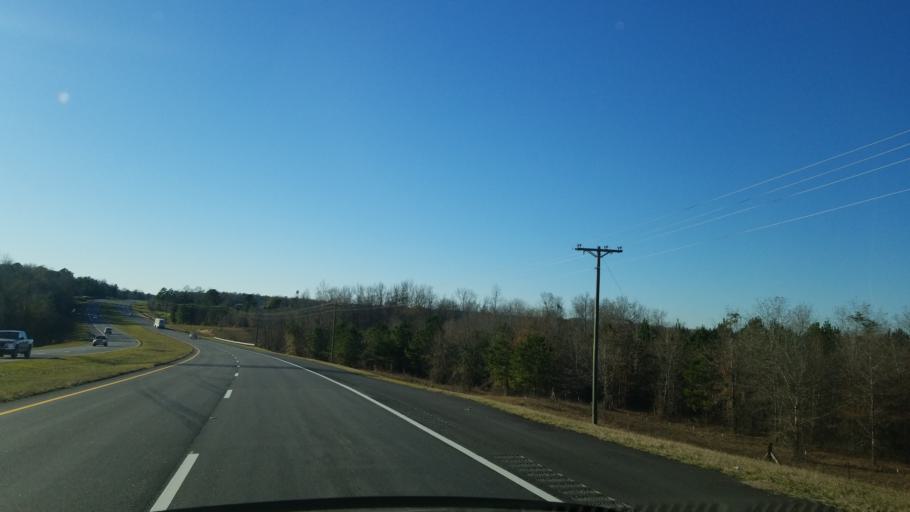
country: US
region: Georgia
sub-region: Talbot County
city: Talbotton
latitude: 32.5756
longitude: -84.5691
